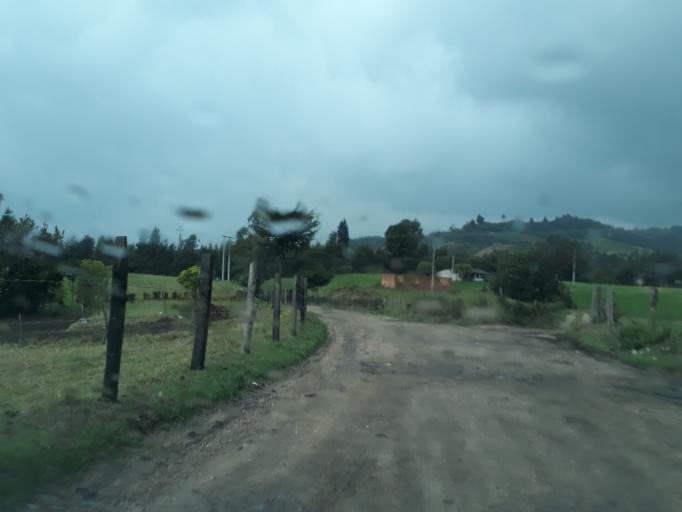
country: CO
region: Boyaca
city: Ventaquemada
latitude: 5.3058
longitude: -73.5828
